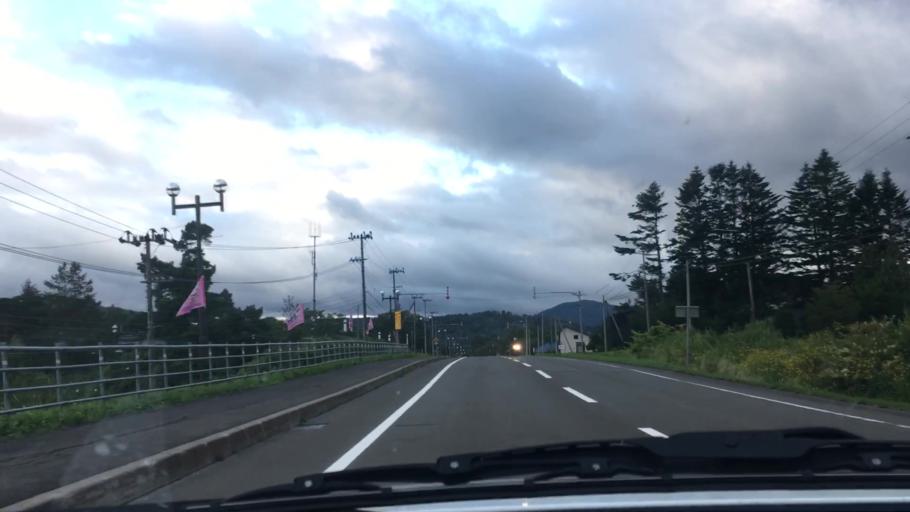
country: JP
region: Hokkaido
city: Shimo-furano
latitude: 42.9921
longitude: 142.4010
